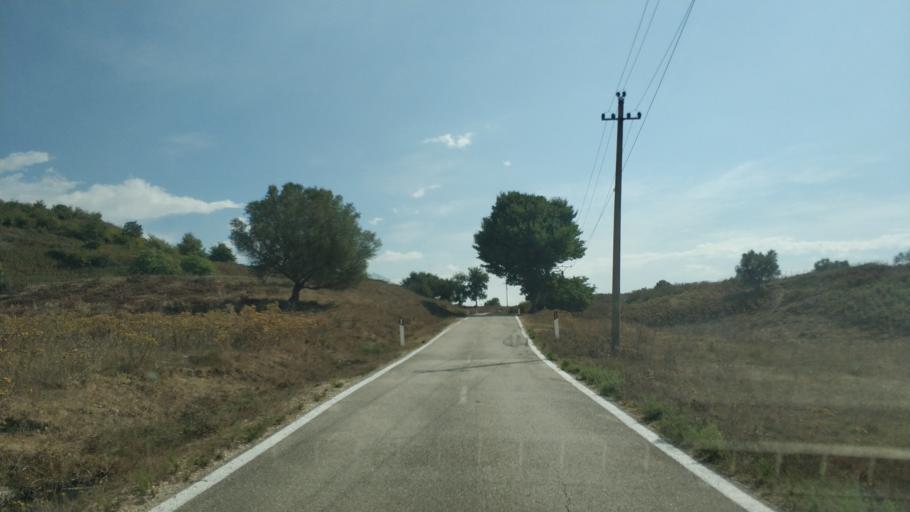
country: AL
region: Fier
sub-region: Rrethi i Fierit
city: Dermenas
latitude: 40.7253
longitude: 19.4686
